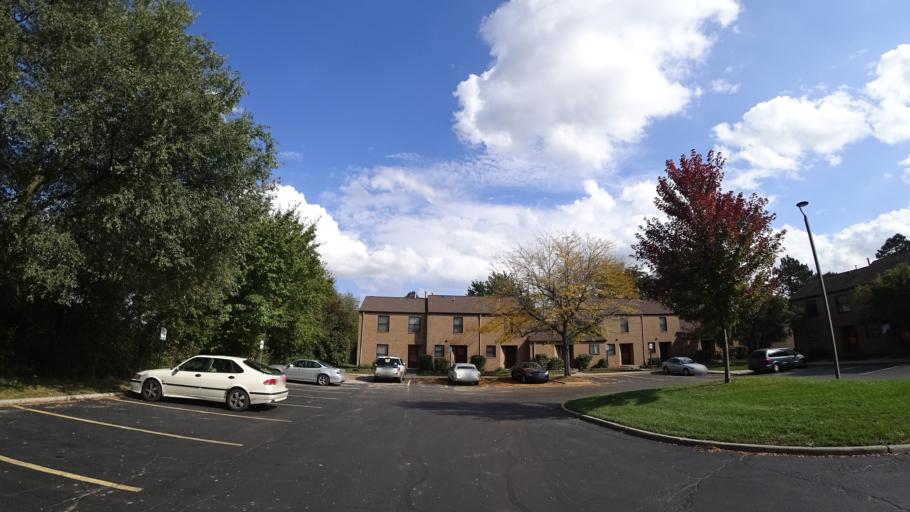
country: US
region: Michigan
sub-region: Saint Joseph County
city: Three Rivers
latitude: 41.9563
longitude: -85.6122
